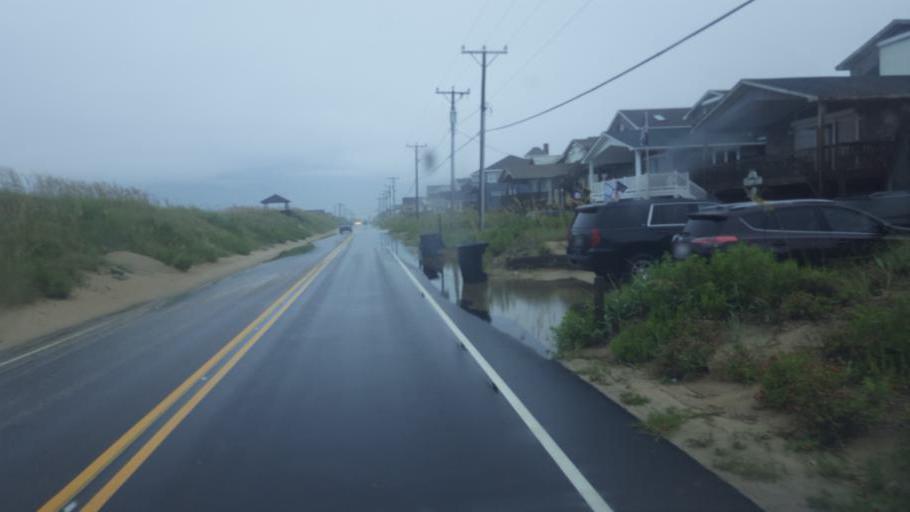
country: US
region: North Carolina
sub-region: Dare County
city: Kitty Hawk
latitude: 36.0647
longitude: -75.6891
